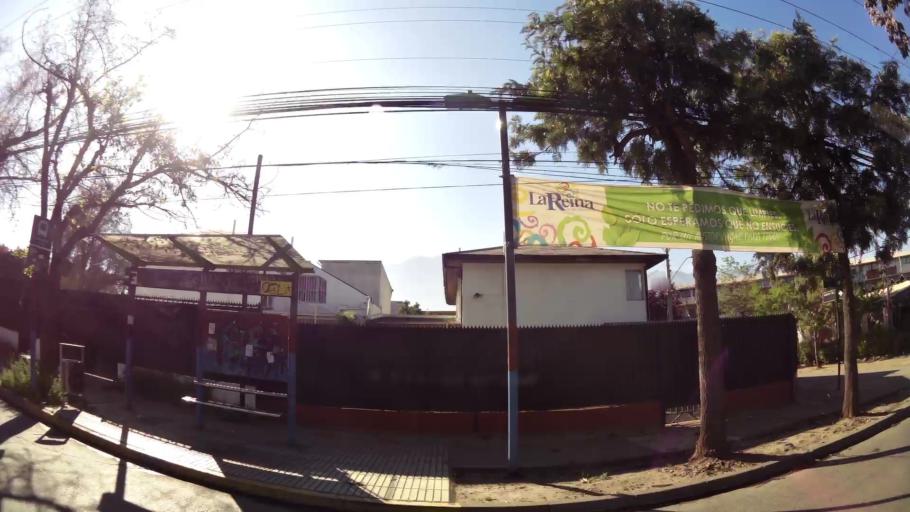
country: CL
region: Santiago Metropolitan
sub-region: Provincia de Santiago
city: Villa Presidente Frei, Nunoa, Santiago, Chile
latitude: -33.4544
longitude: -70.5519
